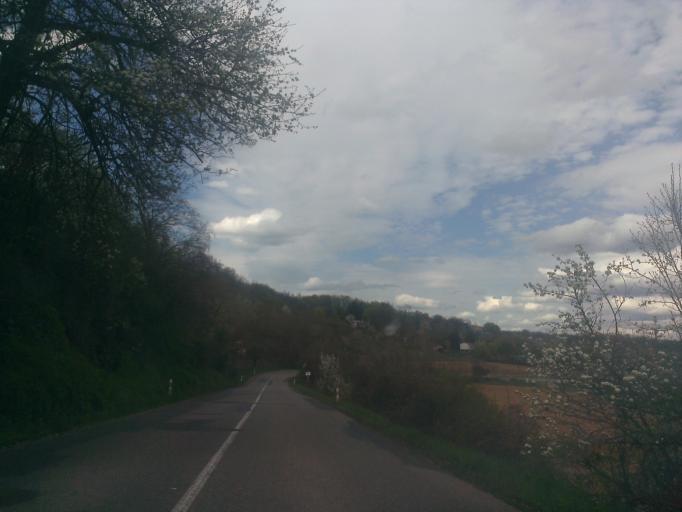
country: CZ
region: South Moravian
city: Dolni Kounice
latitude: 49.1014
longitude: 16.4611
